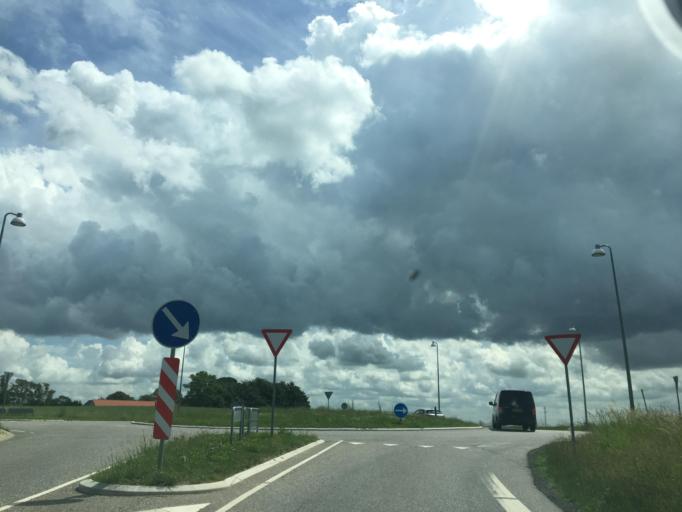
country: DK
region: Zealand
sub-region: Odsherred Kommune
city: Hojby
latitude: 55.8572
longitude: 11.5906
